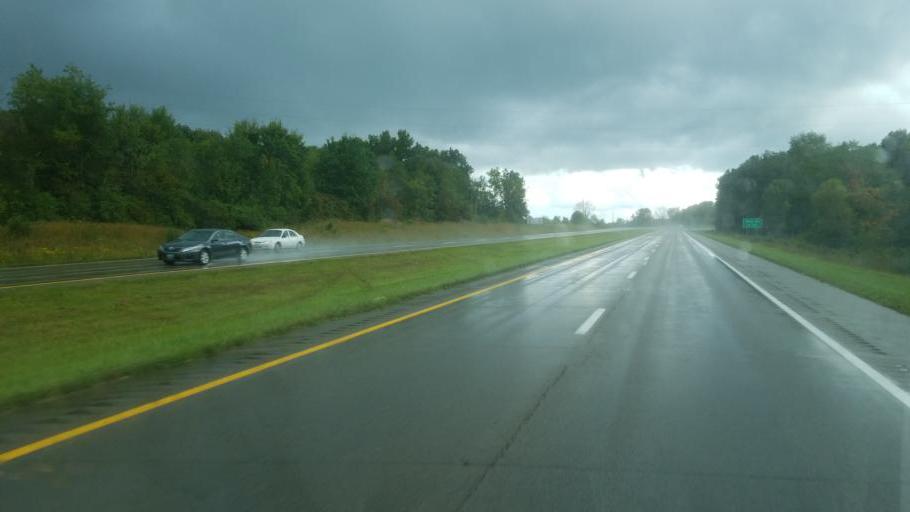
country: US
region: Ohio
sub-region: Jackson County
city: Jackson
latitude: 39.0211
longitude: -82.6429
